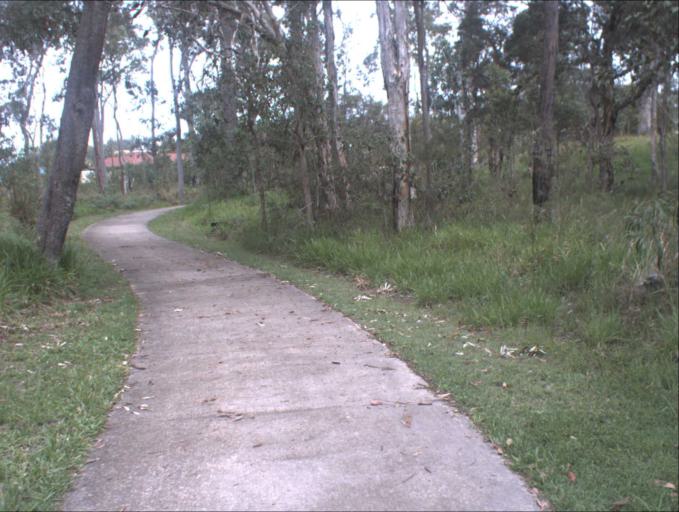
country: AU
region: Queensland
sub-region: Logan
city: Park Ridge South
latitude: -27.6702
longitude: 153.0510
